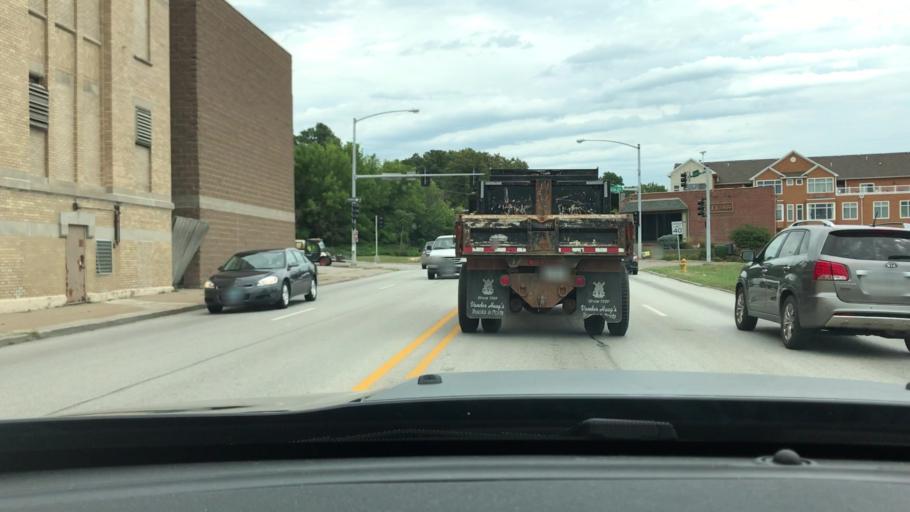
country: US
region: Iowa
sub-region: Scott County
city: Davenport
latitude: 41.5265
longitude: -90.5590
